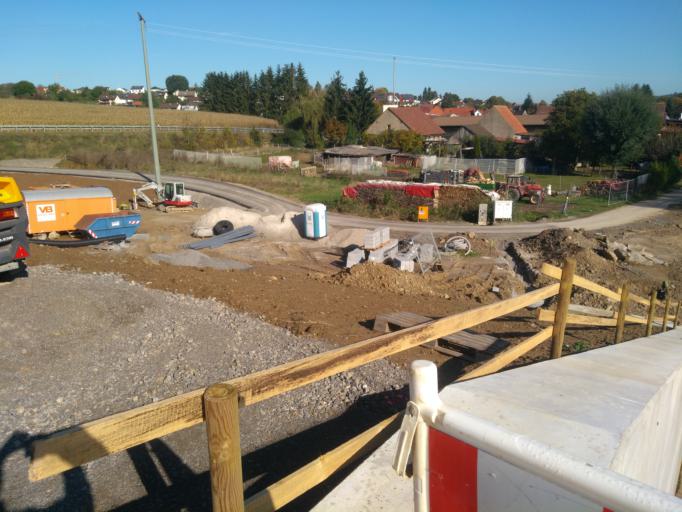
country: DE
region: Baden-Wuerttemberg
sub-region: Karlsruhe Region
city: Konigsbach-Stein
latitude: 48.9230
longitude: 8.5666
